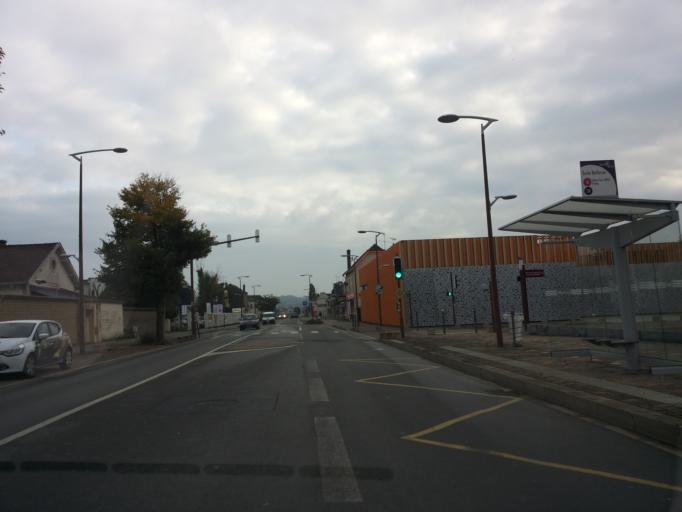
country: FR
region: Champagne-Ardenne
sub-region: Departement des Ardennes
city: Floing
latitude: 49.6962
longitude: 4.9149
